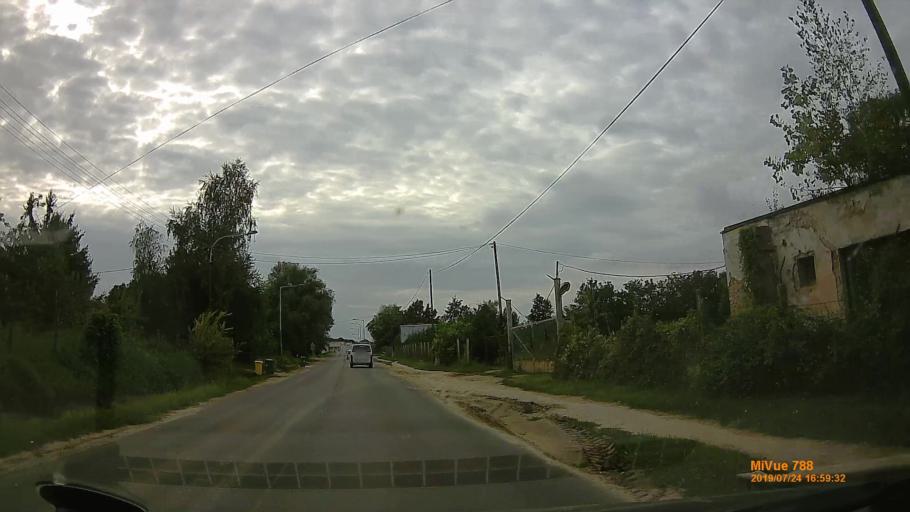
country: HU
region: Borsod-Abauj-Zemplen
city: Tokaj
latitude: 48.1408
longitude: 21.3987
